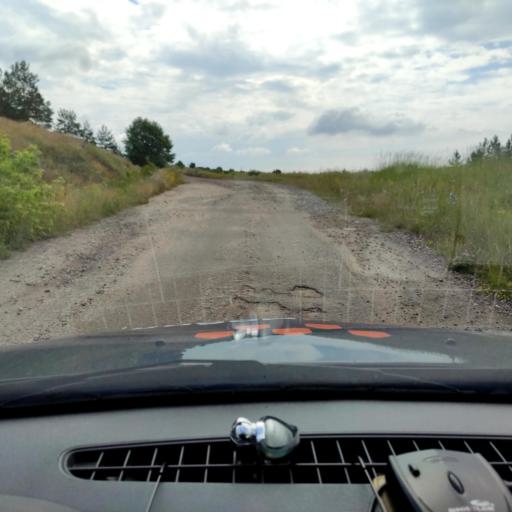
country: RU
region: Voronezj
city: Ramon'
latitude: 52.0746
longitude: 39.3190
